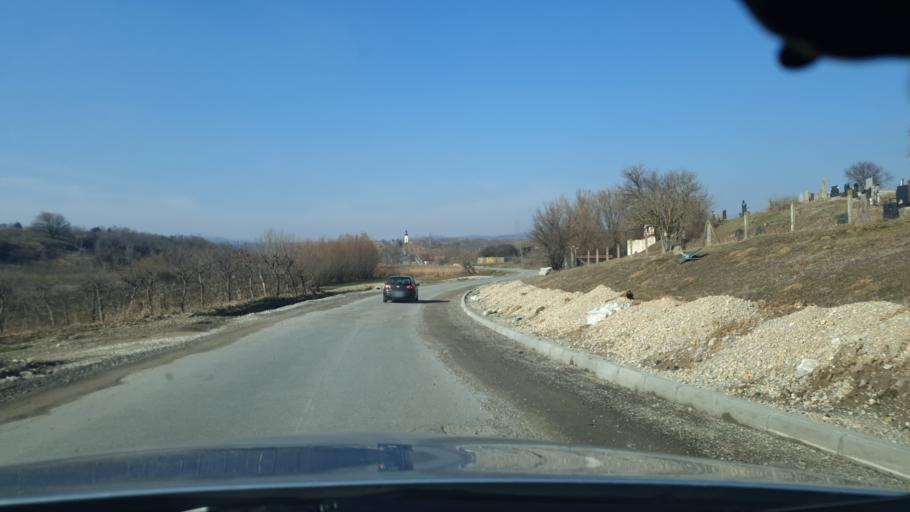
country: RS
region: Autonomna Pokrajina Vojvodina
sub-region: Sremski Okrug
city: Irig
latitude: 45.0816
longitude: 19.8406
